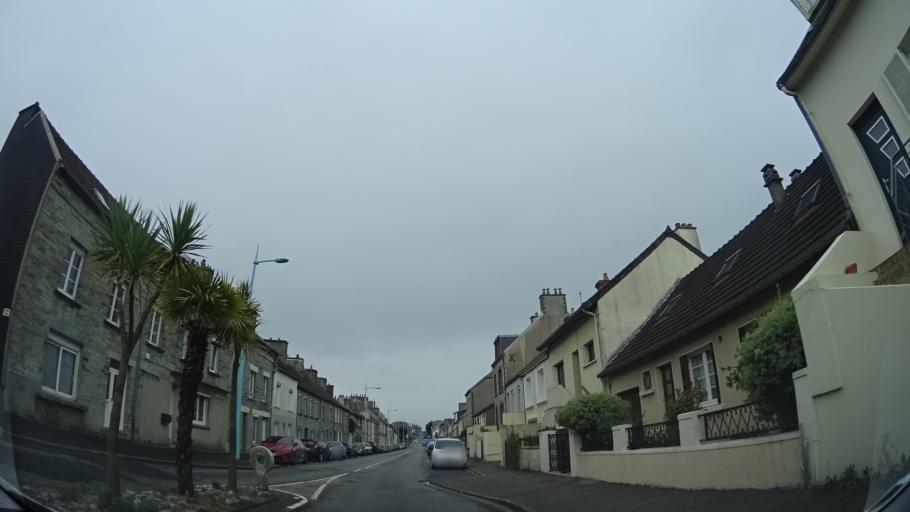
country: FR
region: Lower Normandy
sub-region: Departement de la Manche
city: Octeville
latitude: 49.6308
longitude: -1.6394
